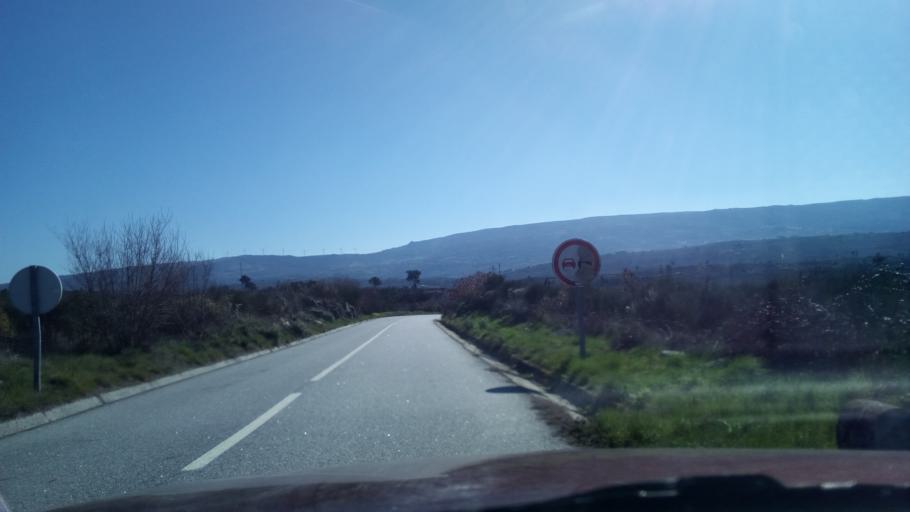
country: PT
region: Guarda
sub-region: Fornos de Algodres
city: Fornos de Algodres
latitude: 40.5998
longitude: -7.5115
